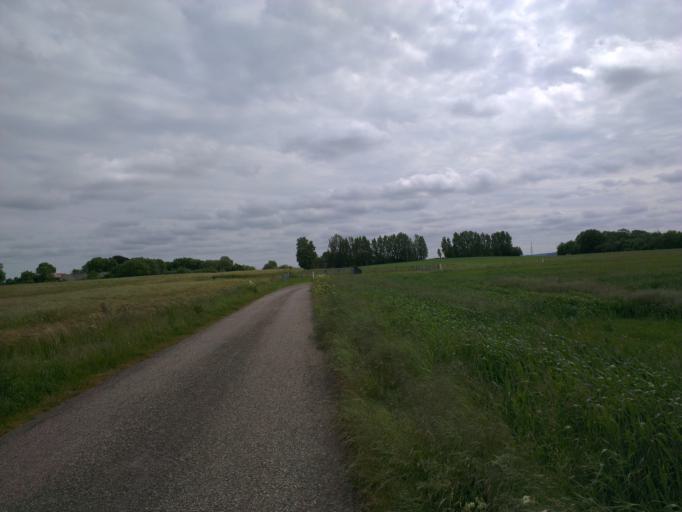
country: DK
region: Capital Region
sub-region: Frederikssund Kommune
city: Frederikssund
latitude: 55.8103
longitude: 12.0791
